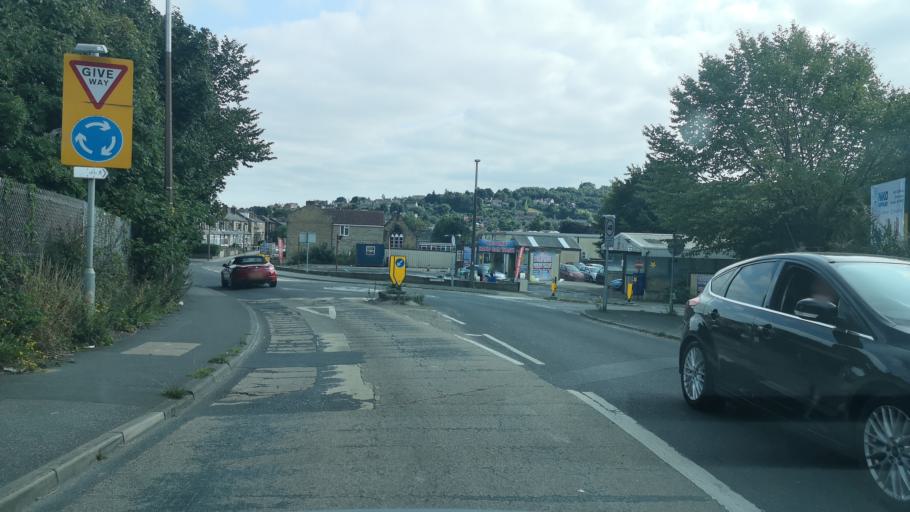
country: GB
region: England
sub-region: Kirklees
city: Dewsbury
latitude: 53.6763
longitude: -1.6351
